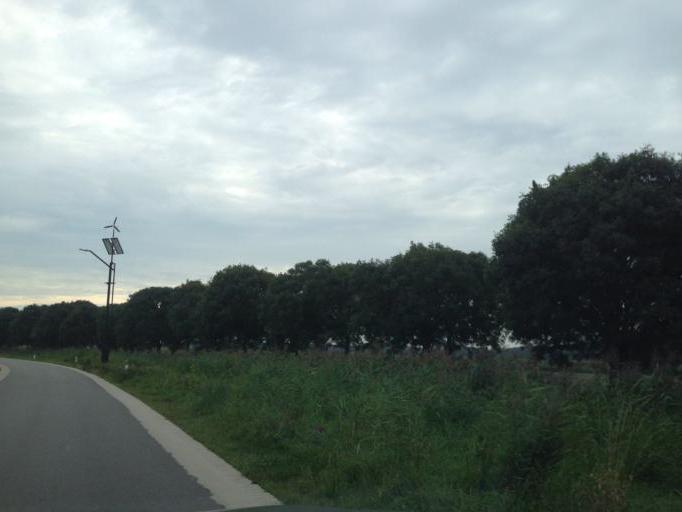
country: NL
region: Flevoland
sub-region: Gemeente Almere
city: Almere Stad
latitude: 52.3682
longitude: 5.2908
